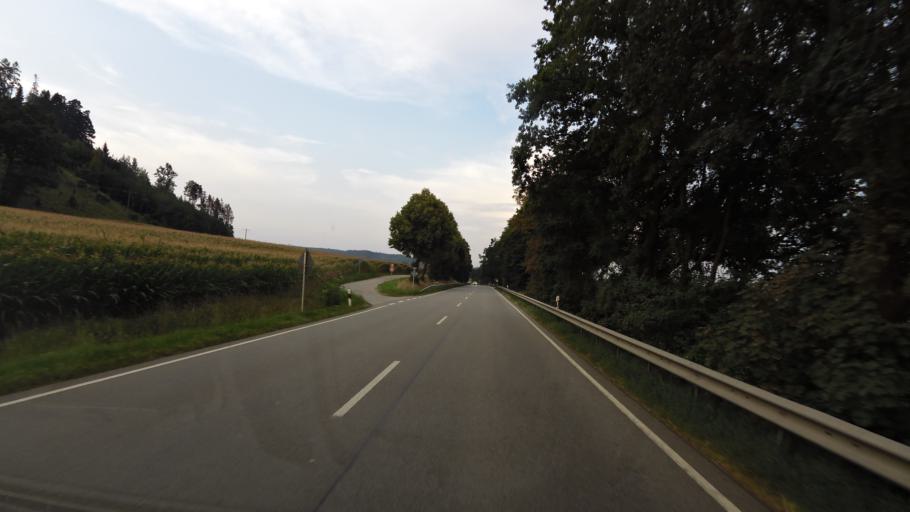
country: DE
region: Bavaria
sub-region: Lower Bavaria
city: Ering
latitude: 48.2943
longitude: 13.1142
